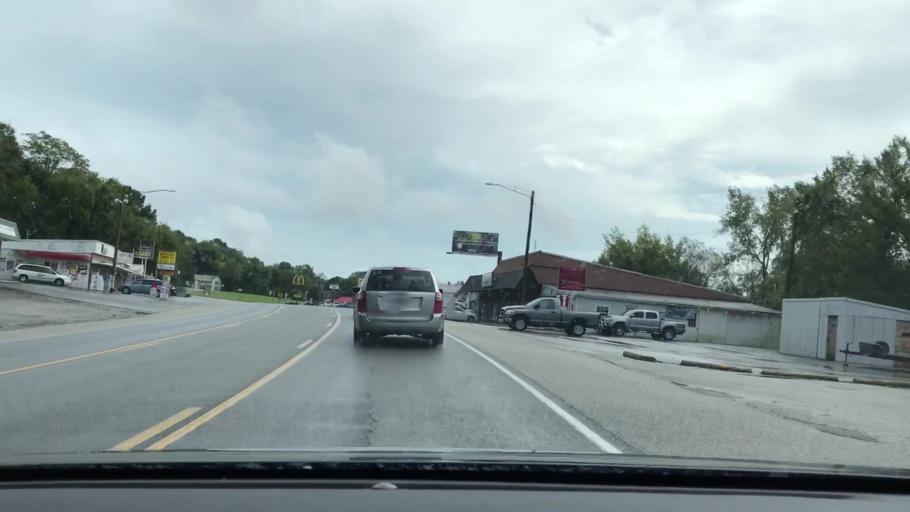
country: US
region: Tennessee
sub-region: Smith County
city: Carthage
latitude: 36.2627
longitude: -85.9546
